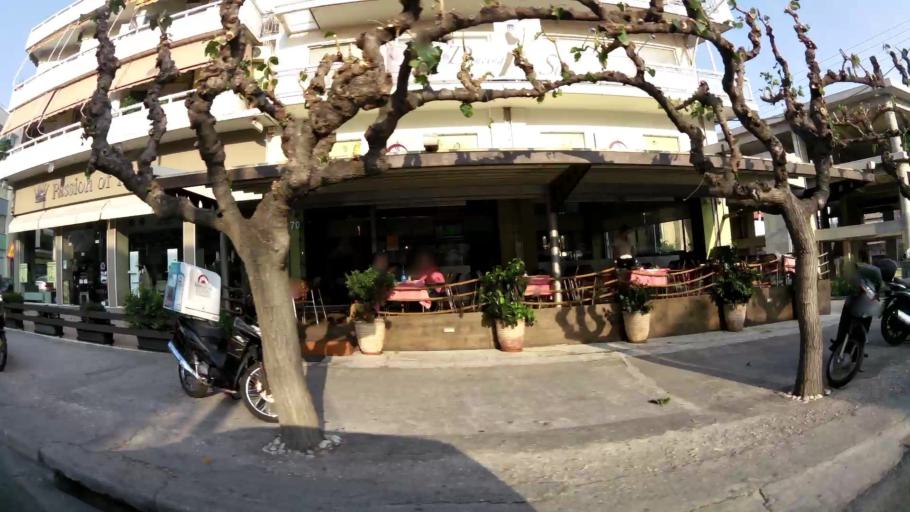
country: GR
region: Attica
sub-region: Nomarchia Athinas
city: Ilion
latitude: 38.0342
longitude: 23.6958
